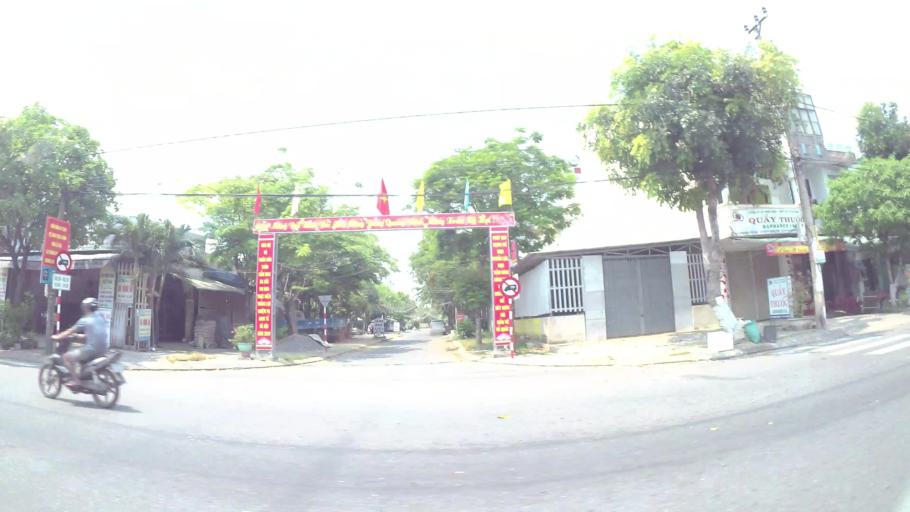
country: VN
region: Da Nang
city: Cam Le
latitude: 16.0021
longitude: 108.2070
